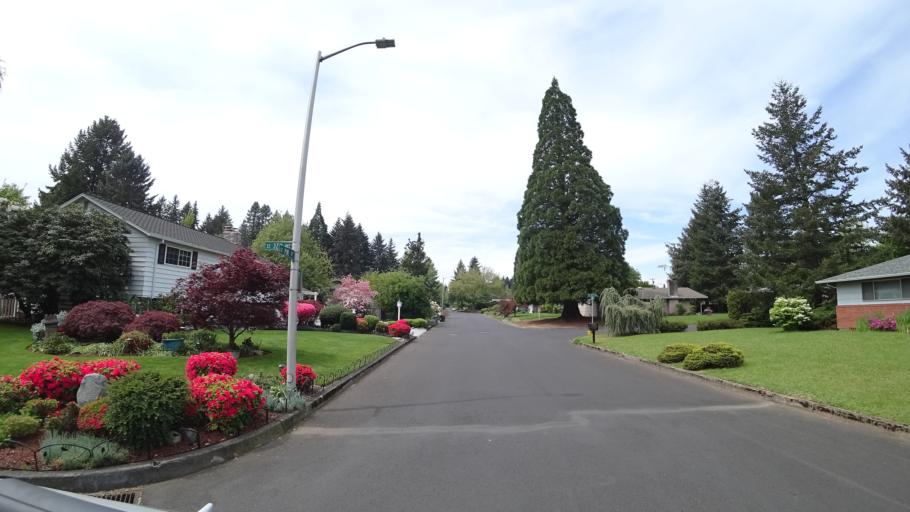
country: US
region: Oregon
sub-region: Washington County
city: Hillsboro
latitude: 45.5115
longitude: -122.9447
